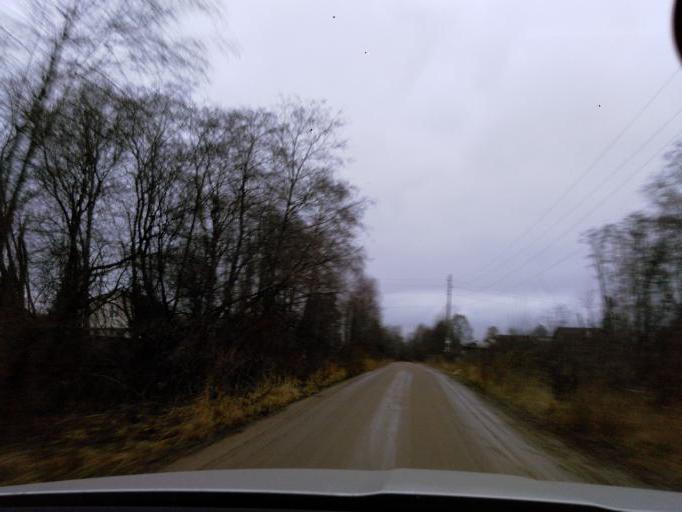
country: RU
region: Moskovskaya
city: Lozhki
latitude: 56.0583
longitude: 37.1085
